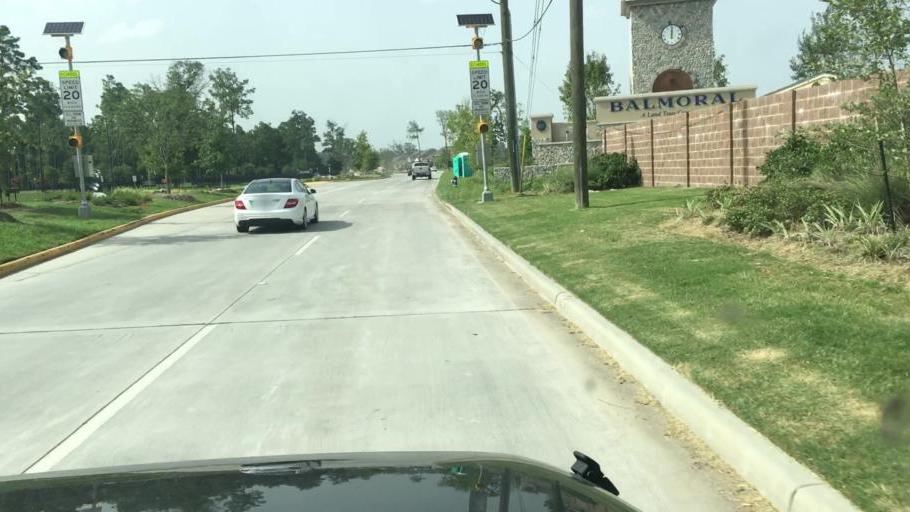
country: US
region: Texas
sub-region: Harris County
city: Atascocita
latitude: 29.9407
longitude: -95.2114
